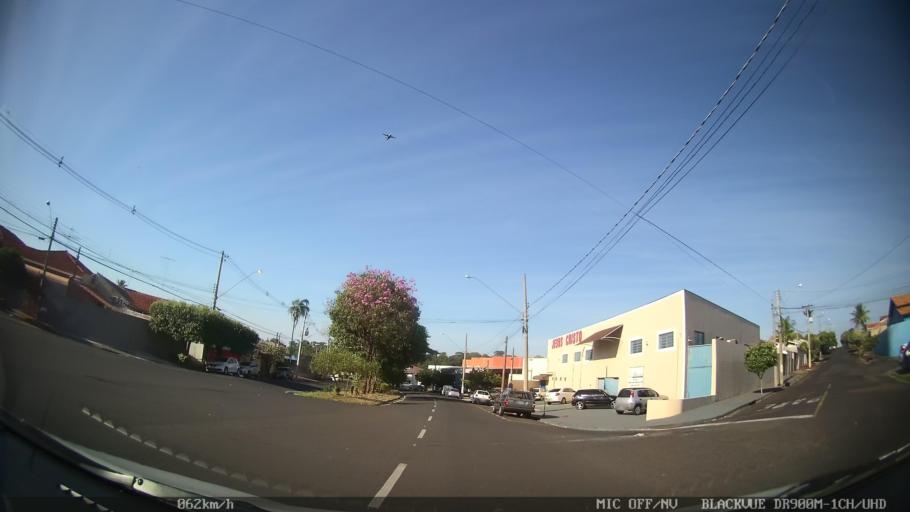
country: BR
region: Sao Paulo
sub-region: Sao Jose Do Rio Preto
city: Sao Jose do Rio Preto
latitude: -20.7794
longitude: -49.3586
